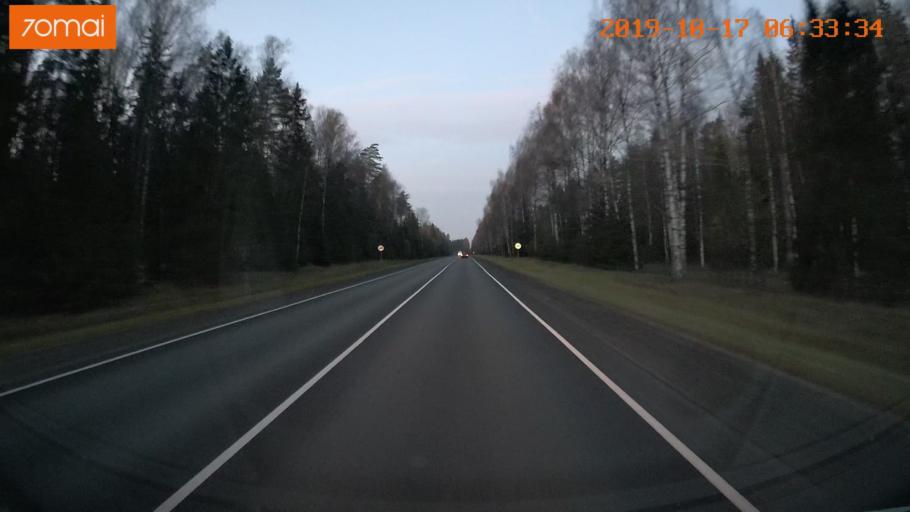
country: RU
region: Ivanovo
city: Novoye Leushino
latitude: 56.7117
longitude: 40.6556
